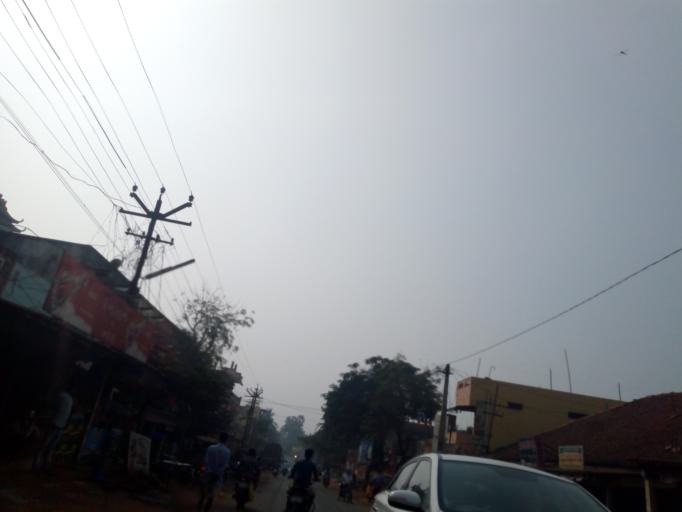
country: IN
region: Andhra Pradesh
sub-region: West Godavari
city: Tadepallegudem
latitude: 16.8194
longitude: 81.4053
